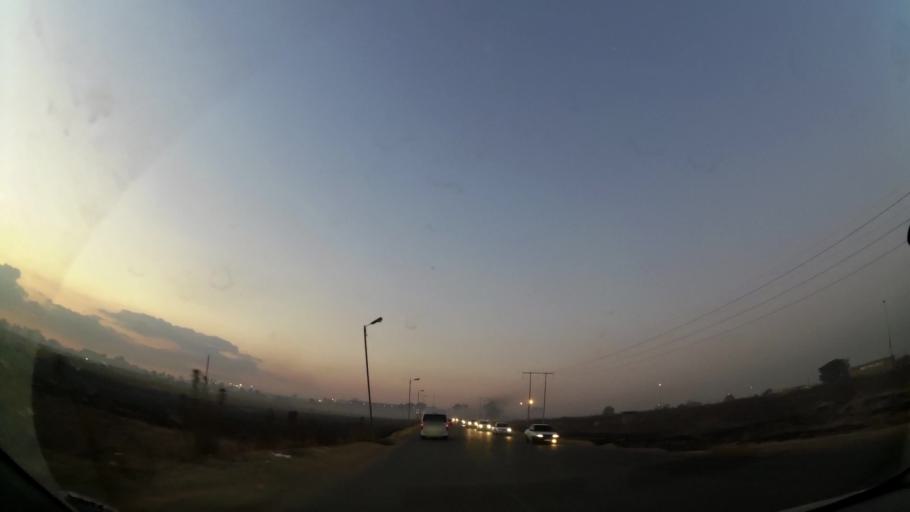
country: ZA
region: Gauteng
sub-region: Ekurhuleni Metropolitan Municipality
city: Springs
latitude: -26.3037
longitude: 28.3805
